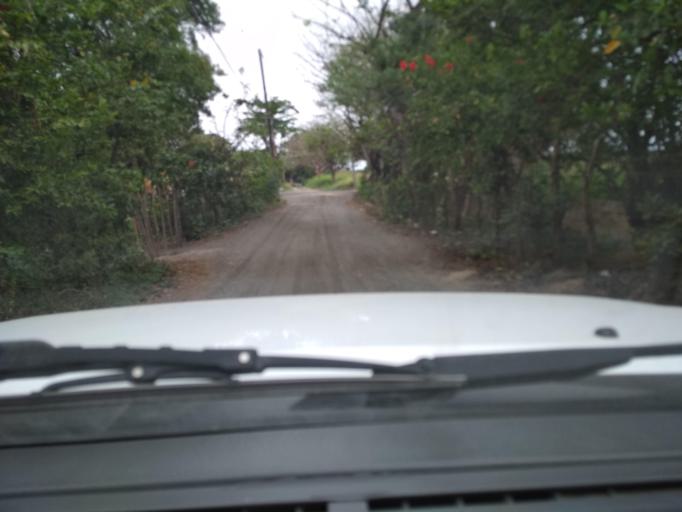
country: MX
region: Veracruz
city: Paso del Toro
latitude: 19.0545
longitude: -96.1341
